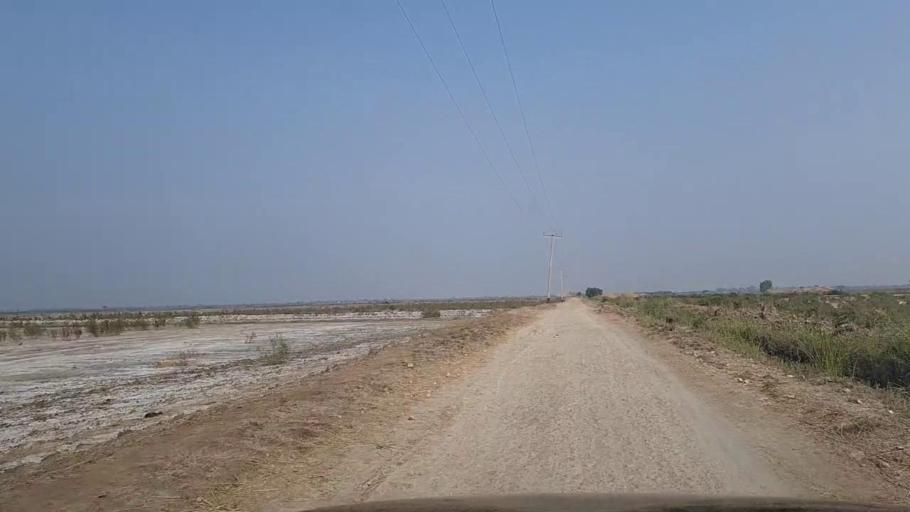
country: PK
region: Sindh
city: Thatta
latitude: 24.7480
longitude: 67.8728
